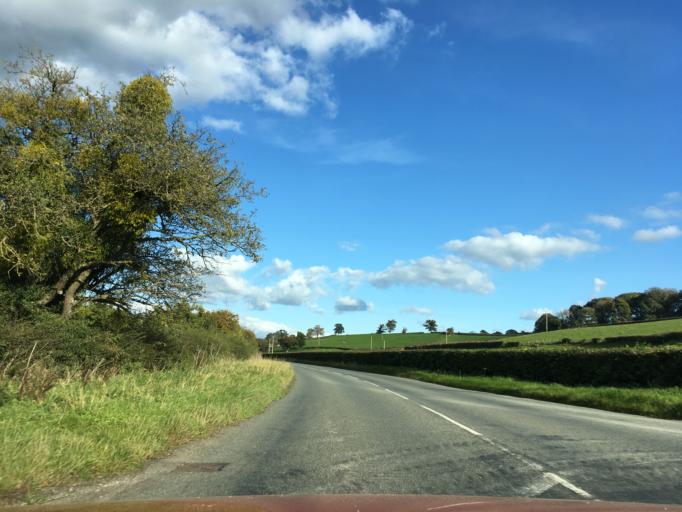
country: GB
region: Wales
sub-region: Sir Powys
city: Hay
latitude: 52.0491
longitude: -3.1834
